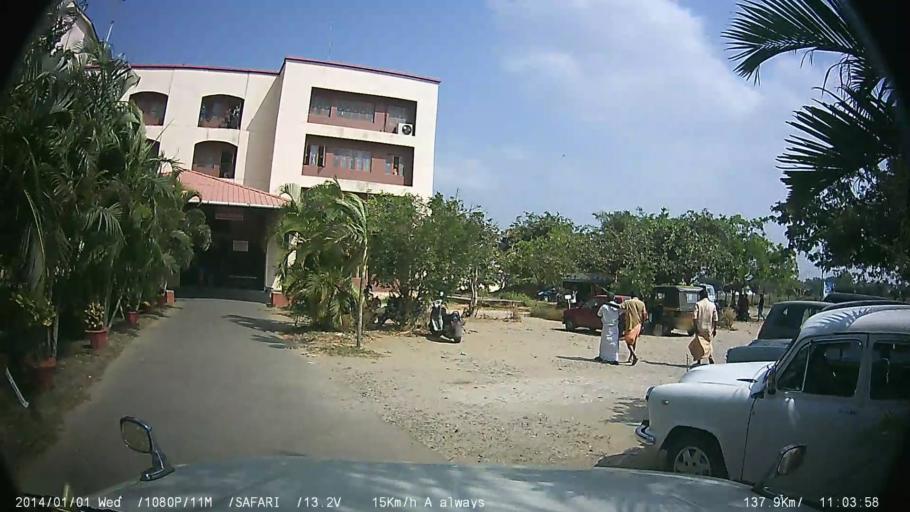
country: IN
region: Kerala
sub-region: Palakkad district
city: Palakkad
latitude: 10.7379
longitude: 76.6517
